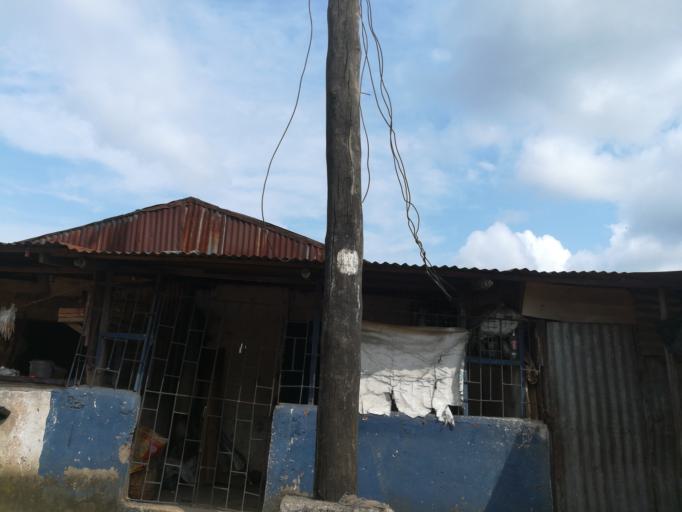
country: NG
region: Rivers
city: Okrika
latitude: 4.7451
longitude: 7.0963
